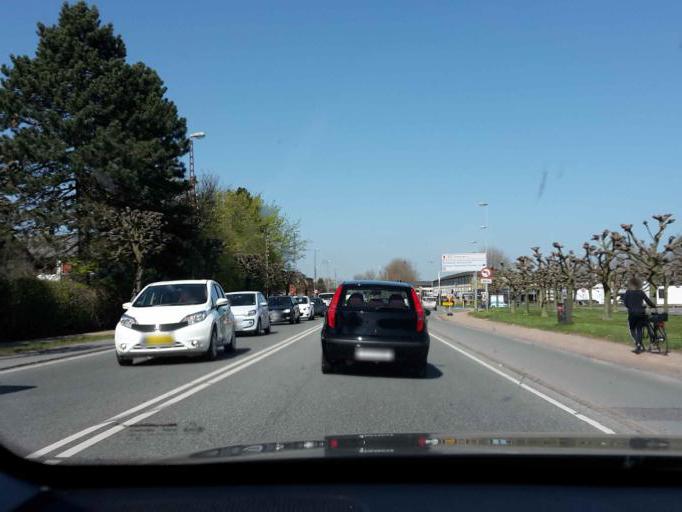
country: DK
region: South Denmark
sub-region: Odense Kommune
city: Odense
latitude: 55.3734
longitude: 10.3958
